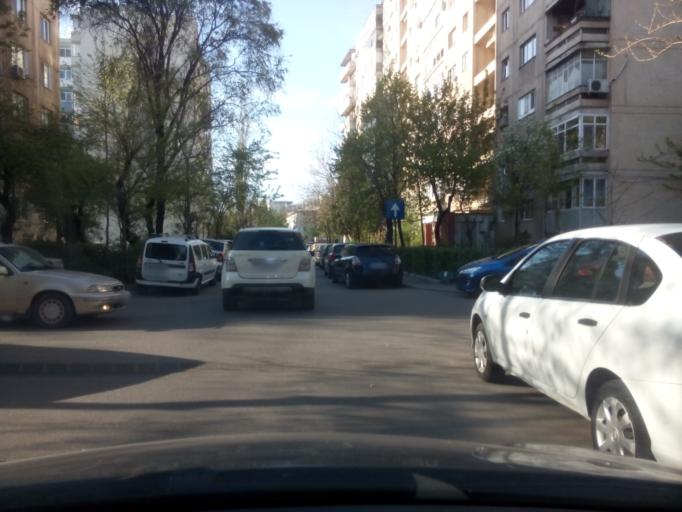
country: RO
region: Ilfov
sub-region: Comuna Fundeni-Dobroesti
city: Fundeni
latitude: 44.4330
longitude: 26.1573
